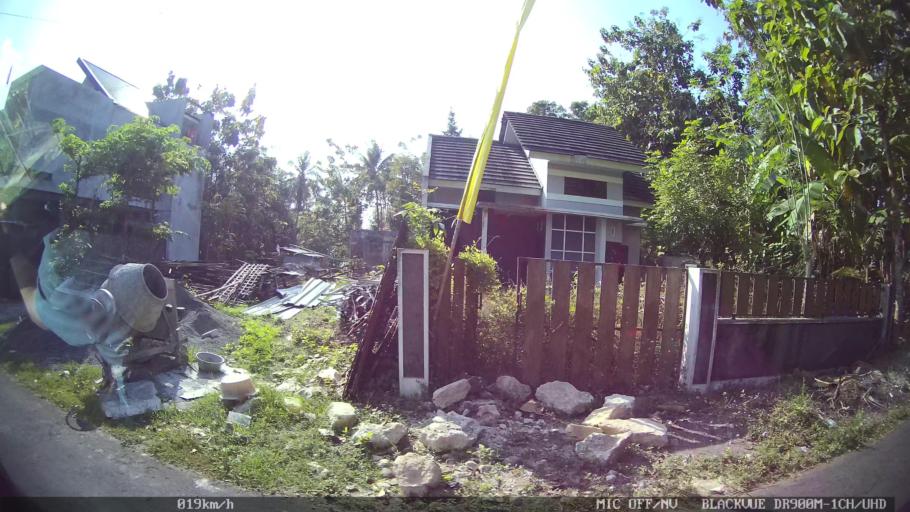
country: ID
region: Daerah Istimewa Yogyakarta
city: Kasihan
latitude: -7.8278
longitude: 110.2883
